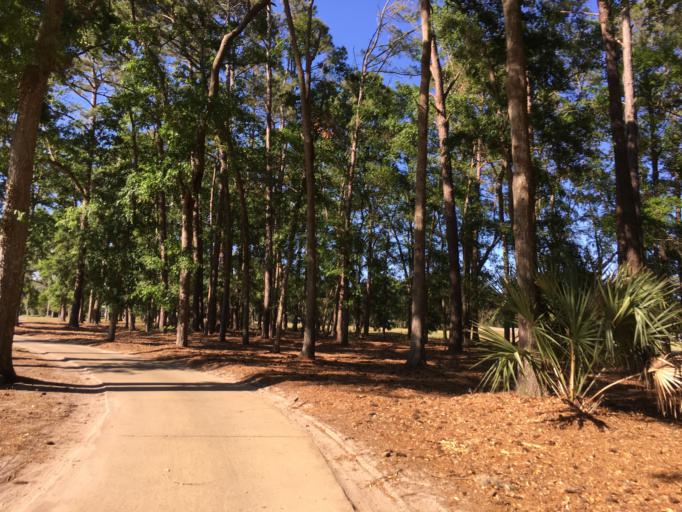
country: US
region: South Carolina
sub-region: Beaufort County
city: Hilton Head Island
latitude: 32.1983
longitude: -80.7451
